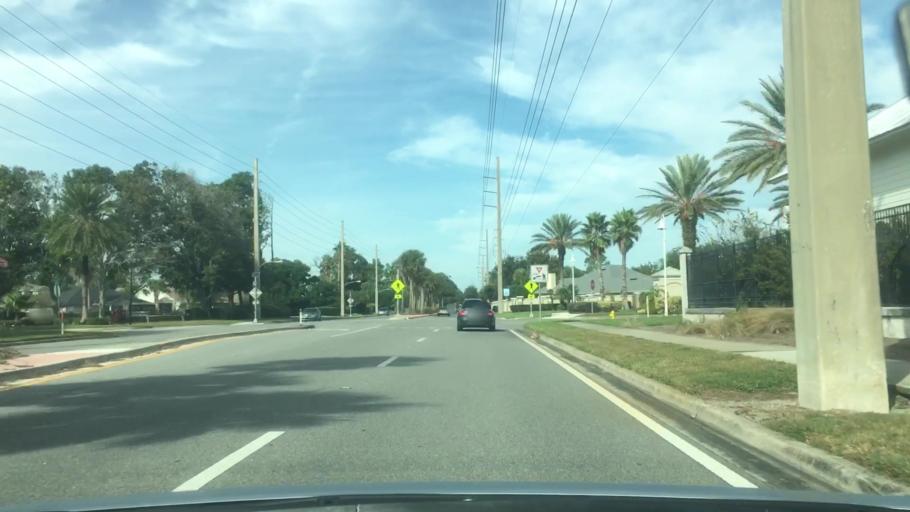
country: US
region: Florida
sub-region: Saint Johns County
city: Ponte Vedra Beach
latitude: 30.2611
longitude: -81.3945
